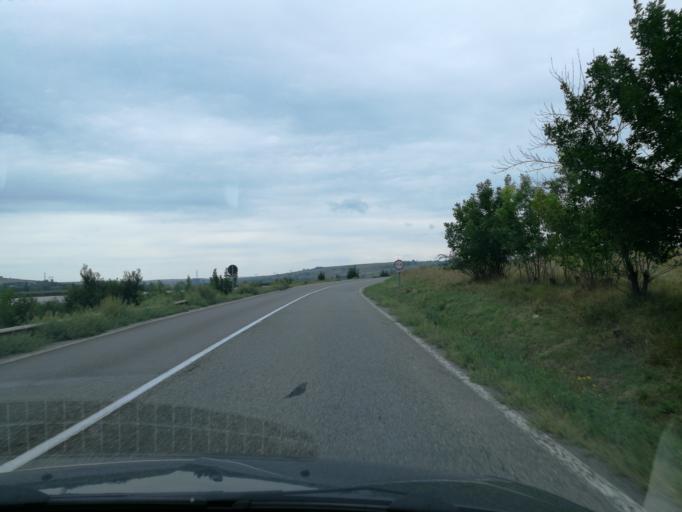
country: RO
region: Suceava
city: Bunesti-Regat
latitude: 47.4951
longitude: 26.2821
